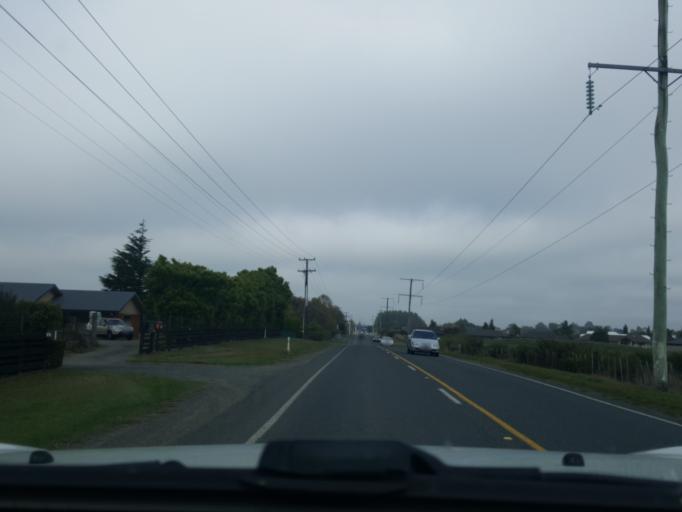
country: NZ
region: Waikato
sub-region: Hamilton City
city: Hamilton
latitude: -37.7421
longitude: 175.2903
